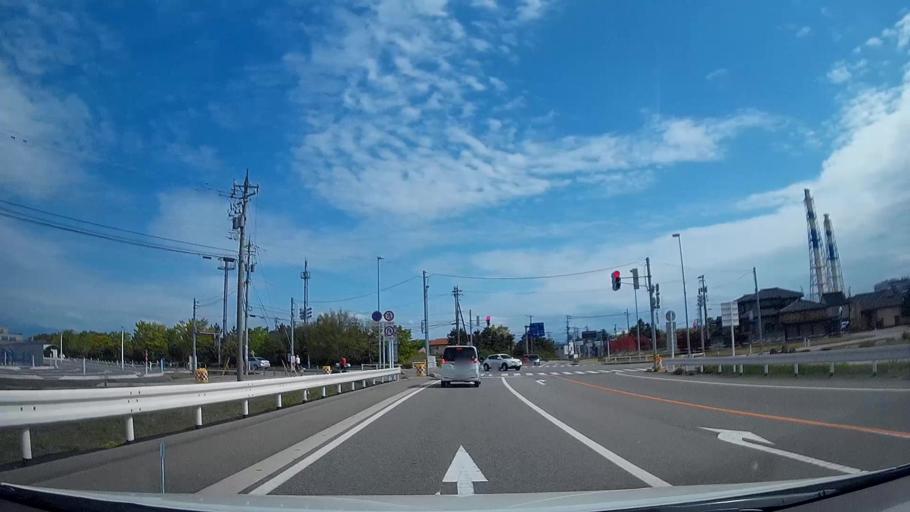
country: JP
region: Toyama
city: Kuragaki-kosugi
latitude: 36.7707
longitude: 137.1342
